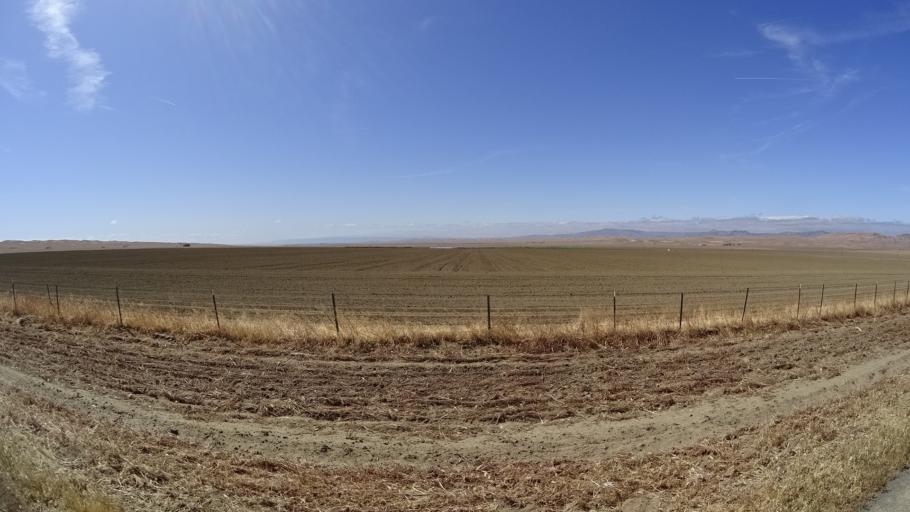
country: US
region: California
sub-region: Kings County
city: Kettleman City
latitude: 35.9352
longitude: -120.0344
